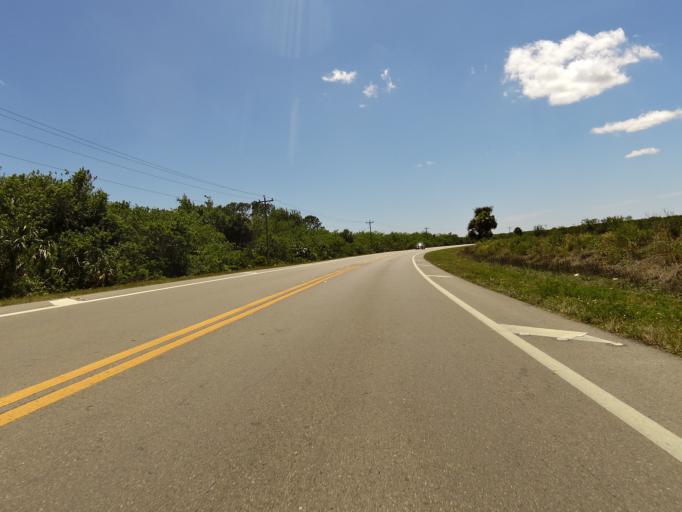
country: US
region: Florida
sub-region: Collier County
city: Immokalee
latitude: 26.3692
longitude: -81.4190
